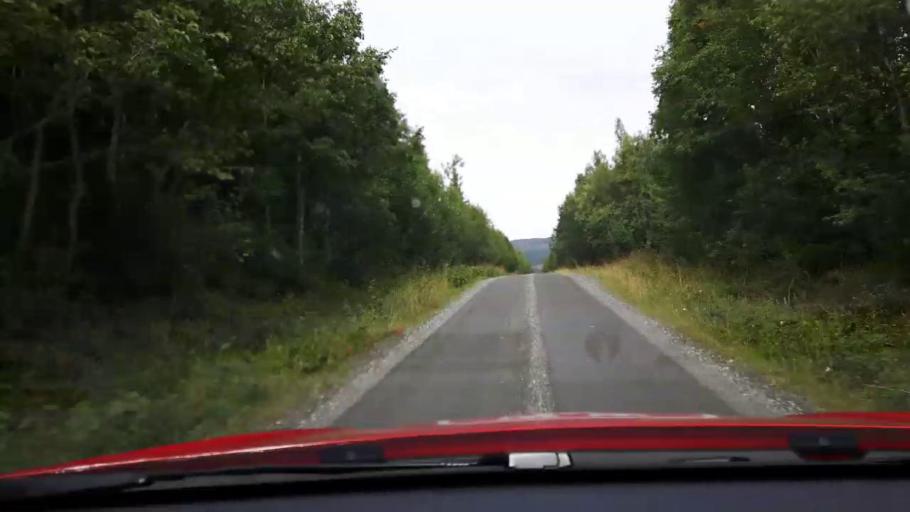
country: SE
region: Jaemtland
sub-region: Are Kommun
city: Are
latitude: 63.7859
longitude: 13.1045
